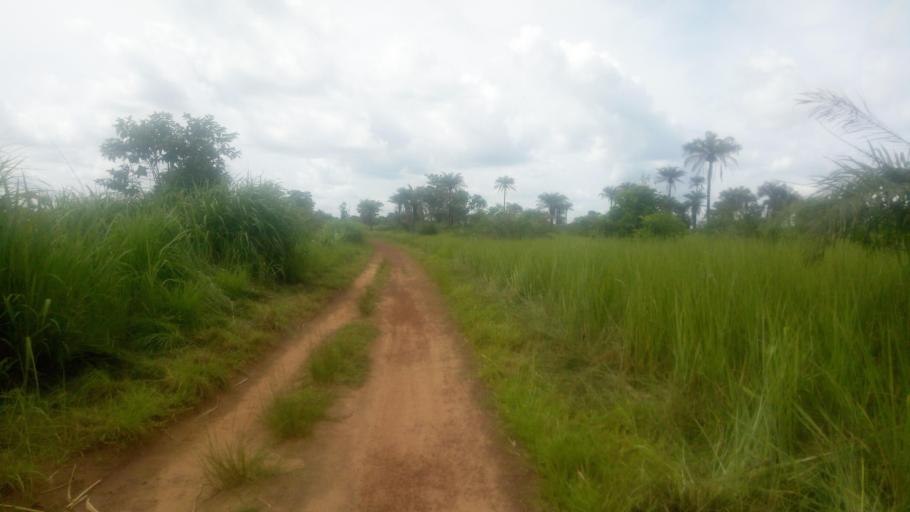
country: SL
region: Northern Province
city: Magburaka
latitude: 8.6807
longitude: -12.0674
